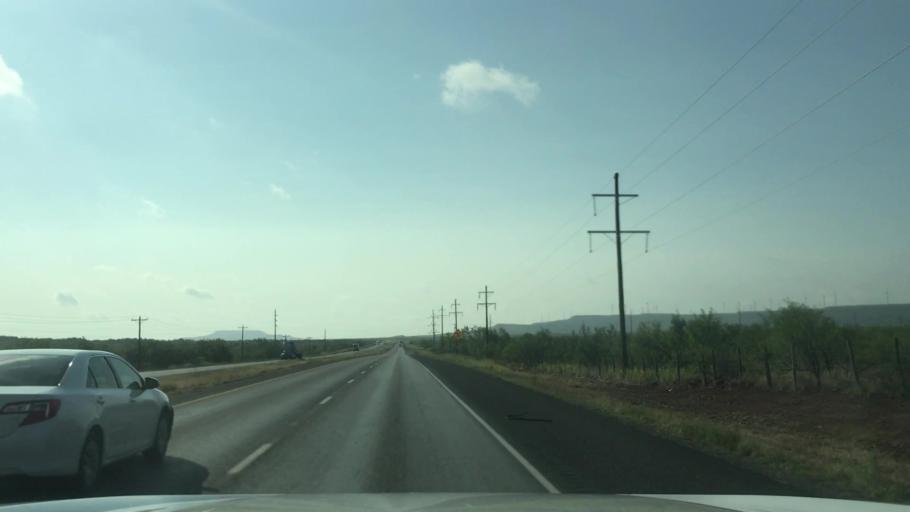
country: US
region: Texas
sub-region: Garza County
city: Post
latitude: 32.9981
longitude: -101.1550
